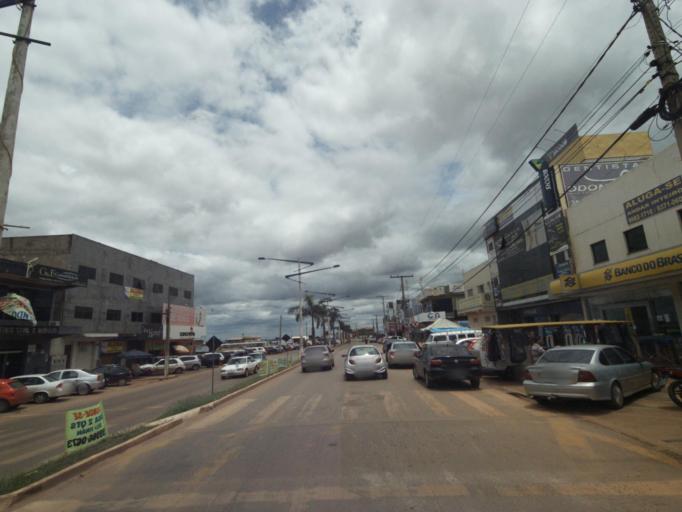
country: BR
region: Federal District
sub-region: Brasilia
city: Brasilia
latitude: -15.7343
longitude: -48.2834
